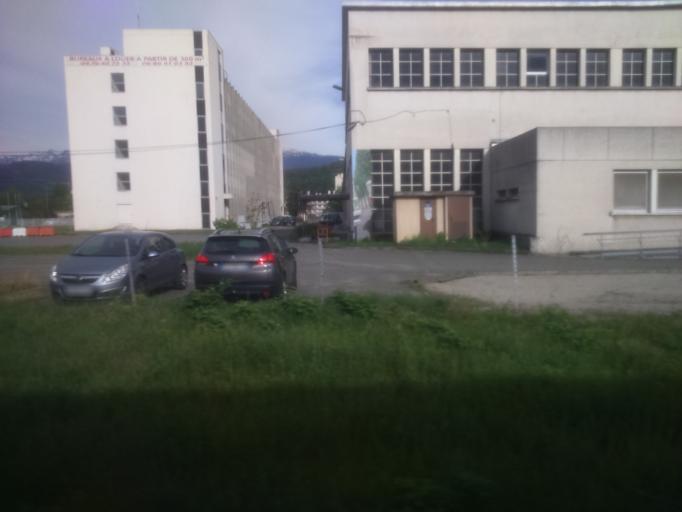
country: FR
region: Rhone-Alpes
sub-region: Departement de l'Isere
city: Le Pont-de-Claix
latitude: 45.1372
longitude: 5.7030
